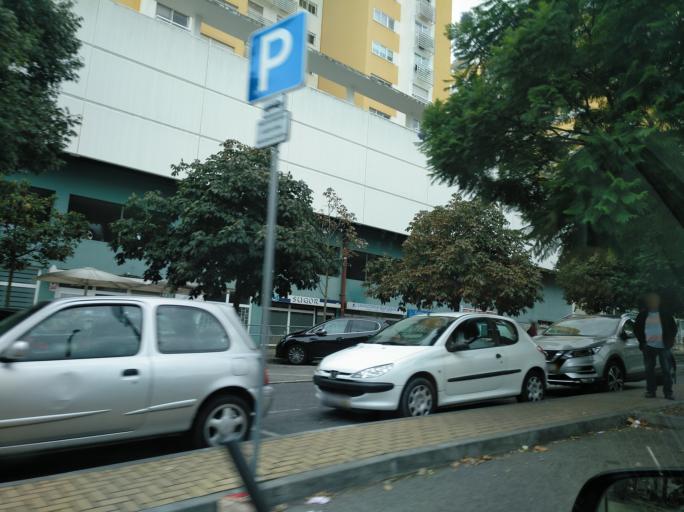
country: PT
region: Lisbon
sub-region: Lisbon
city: Lisbon
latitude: 38.7279
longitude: -9.1251
